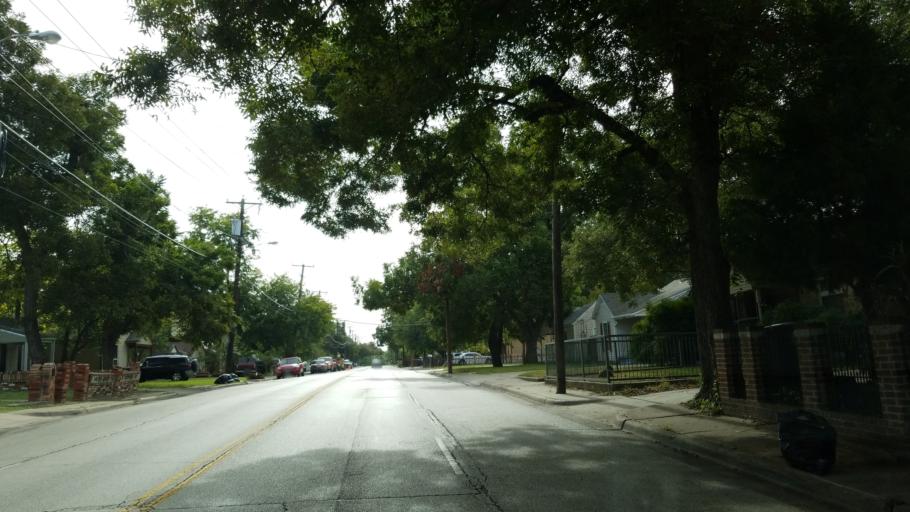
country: US
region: Texas
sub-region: Dallas County
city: Dallas
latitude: 32.7832
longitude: -96.7214
